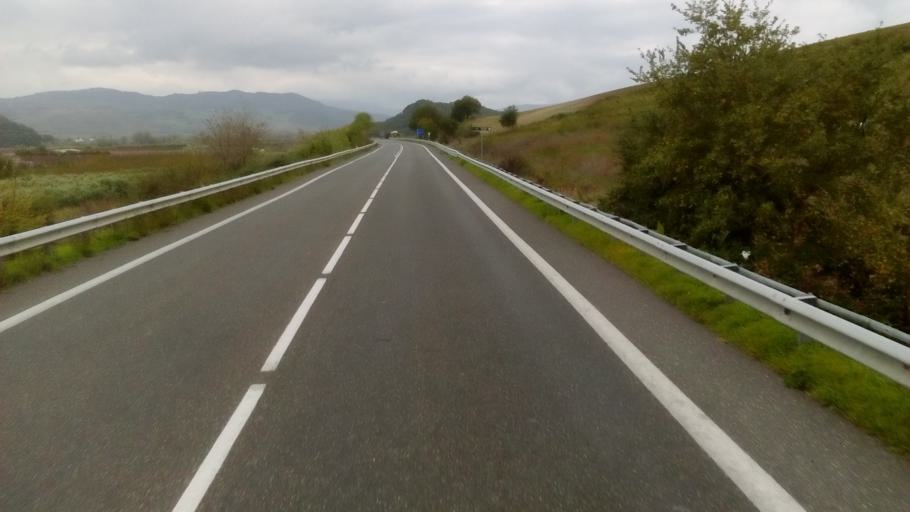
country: IT
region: Abruzzo
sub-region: Provincia di Chieti
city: San Salvo
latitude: 42.0124
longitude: 14.7251
